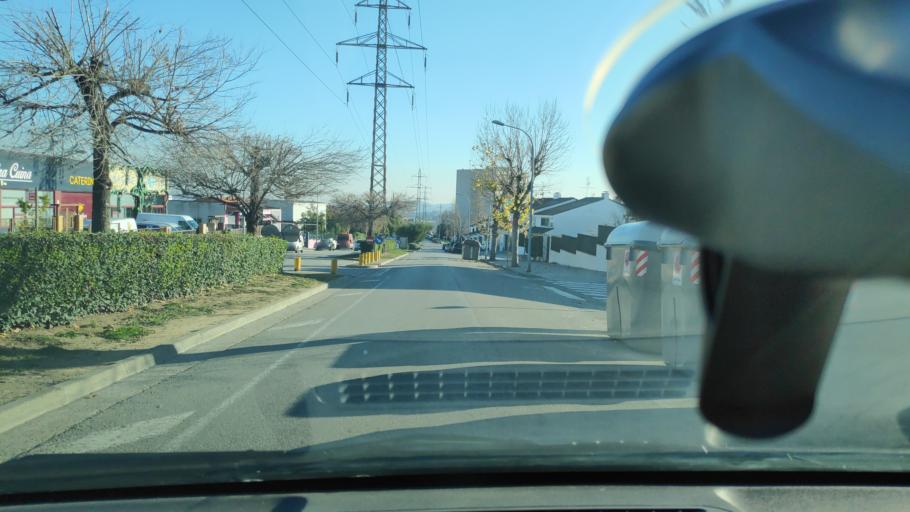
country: ES
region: Catalonia
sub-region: Provincia de Barcelona
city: Sant Quirze del Valles
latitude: 41.5388
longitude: 2.0731
